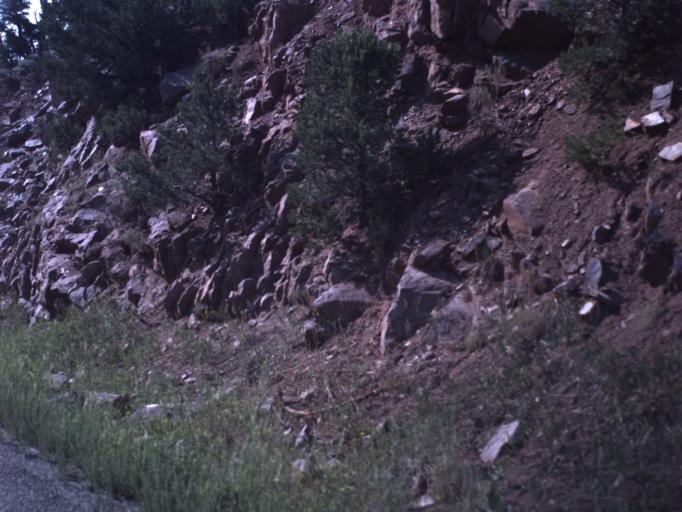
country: US
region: Utah
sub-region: Daggett County
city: Manila
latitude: 40.9395
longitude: -109.4096
